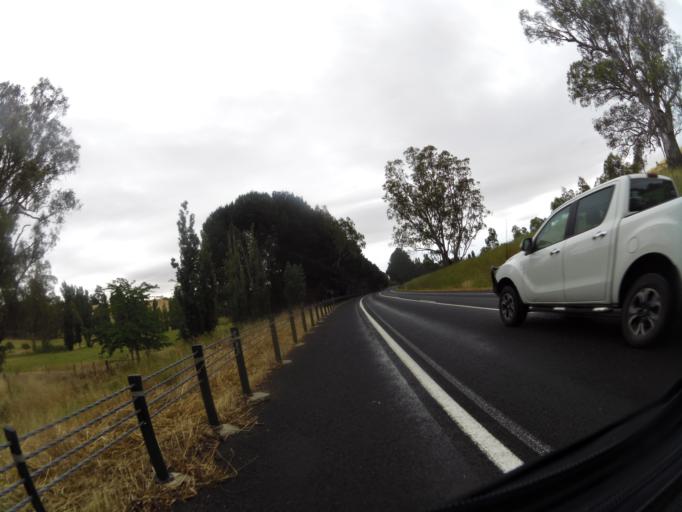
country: AU
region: Victoria
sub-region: Mount Alexander
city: Castlemaine
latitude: -37.1820
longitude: 144.0273
